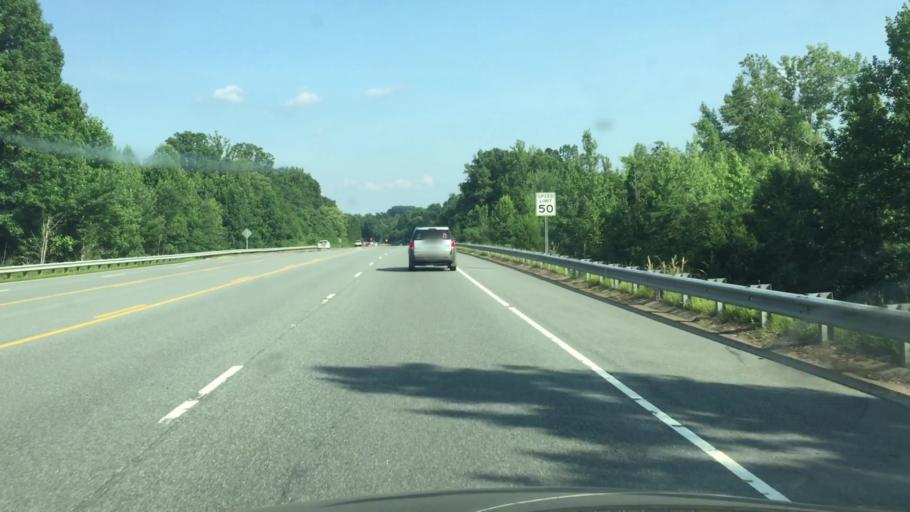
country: US
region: North Carolina
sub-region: Rockingham County
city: Reidsville
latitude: 36.3681
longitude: -79.6440
